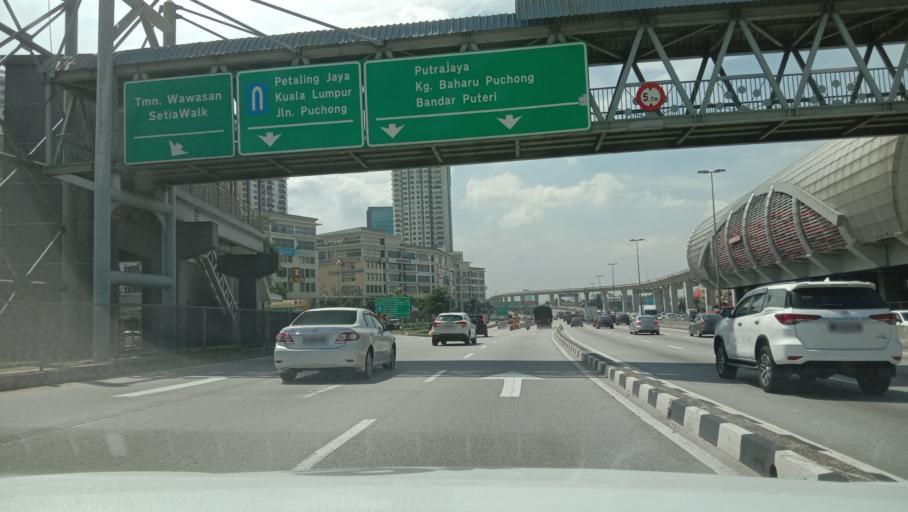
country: MY
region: Selangor
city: Subang Jaya
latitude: 3.0339
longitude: 101.6168
